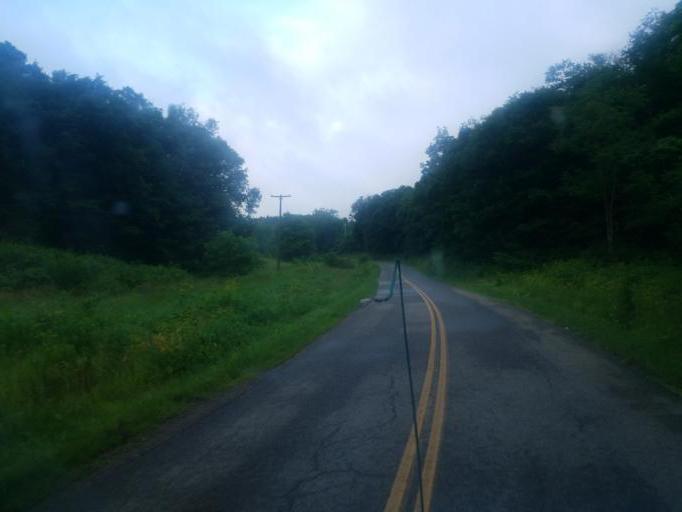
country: US
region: Ohio
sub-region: Columbiana County
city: Salineville
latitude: 40.5777
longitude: -80.9494
